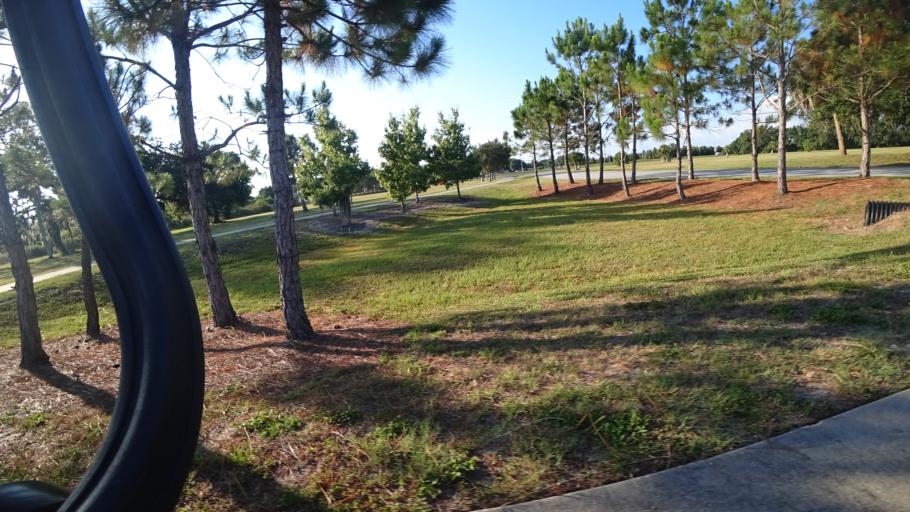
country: US
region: Florida
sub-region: Manatee County
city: Ellenton
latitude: 27.5003
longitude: -82.4830
